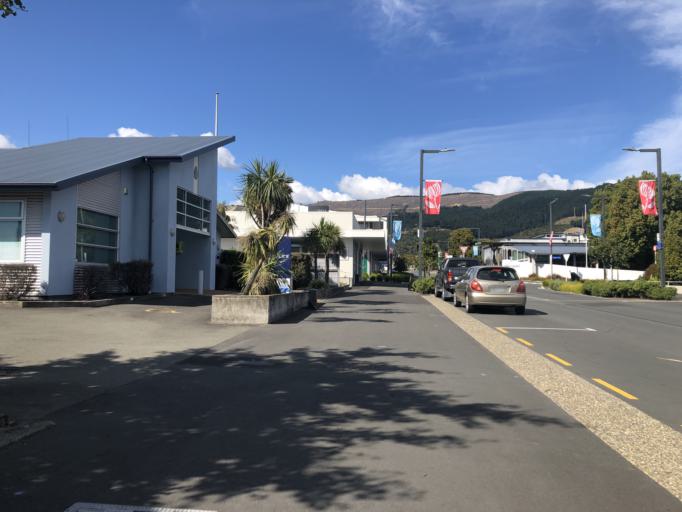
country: NZ
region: Tasman
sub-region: Tasman District
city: Richmond
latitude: -41.3408
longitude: 173.1864
